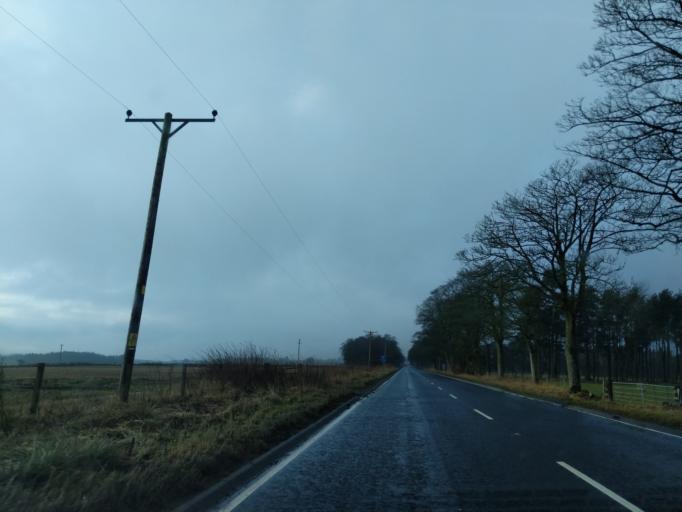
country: GB
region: Scotland
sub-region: Perth and Kinross
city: Kinross
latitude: 56.2029
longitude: -3.4817
